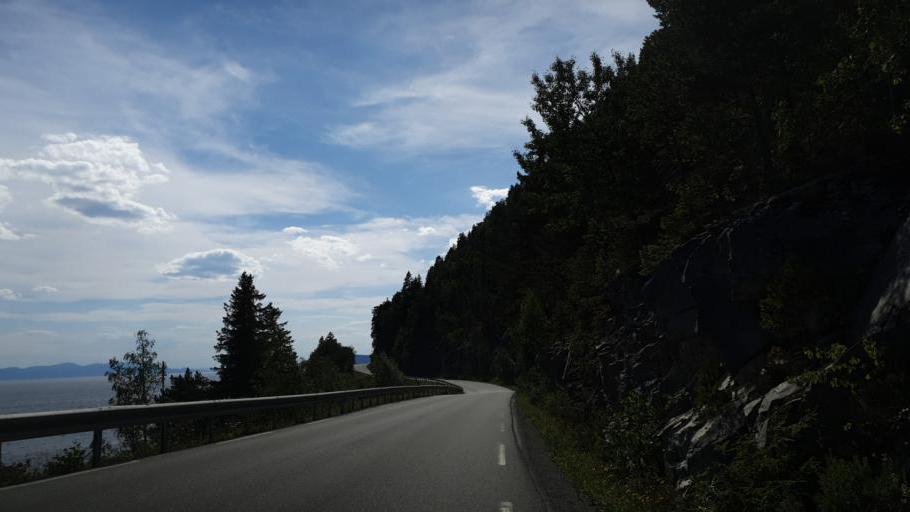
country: NO
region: Nord-Trondelag
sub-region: Leksvik
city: Leksvik
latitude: 63.6287
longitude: 10.5648
